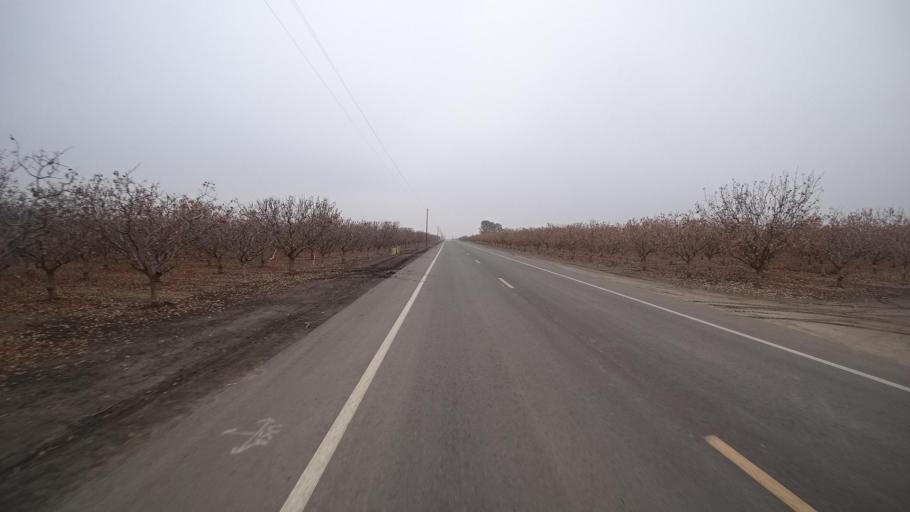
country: US
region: California
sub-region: Kern County
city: Buttonwillow
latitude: 35.3692
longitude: -119.4521
